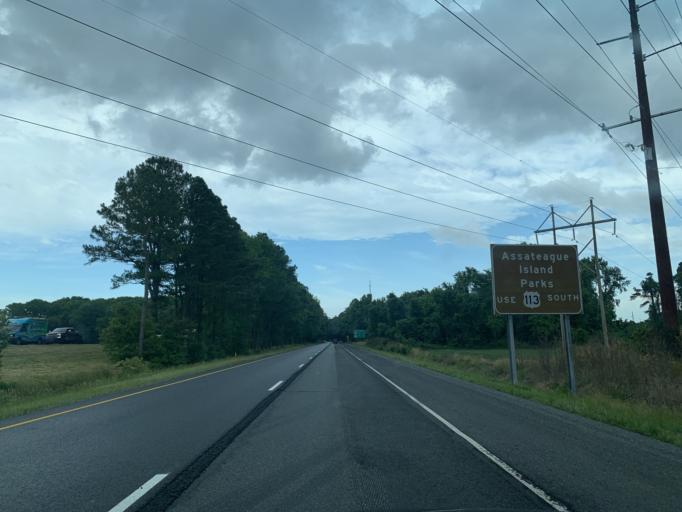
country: US
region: Maryland
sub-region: Worcester County
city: Berlin
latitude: 38.3481
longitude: -75.2318
